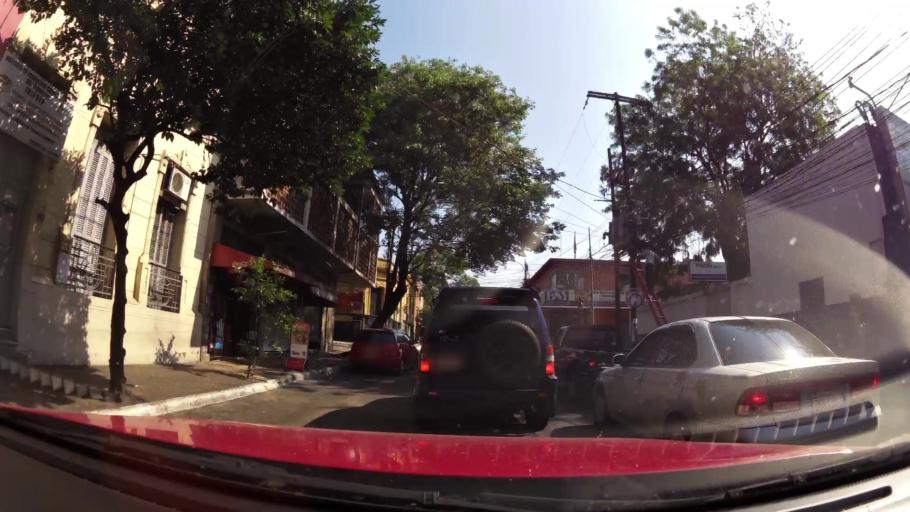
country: PY
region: Asuncion
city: Asuncion
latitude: -25.2905
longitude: -57.6284
